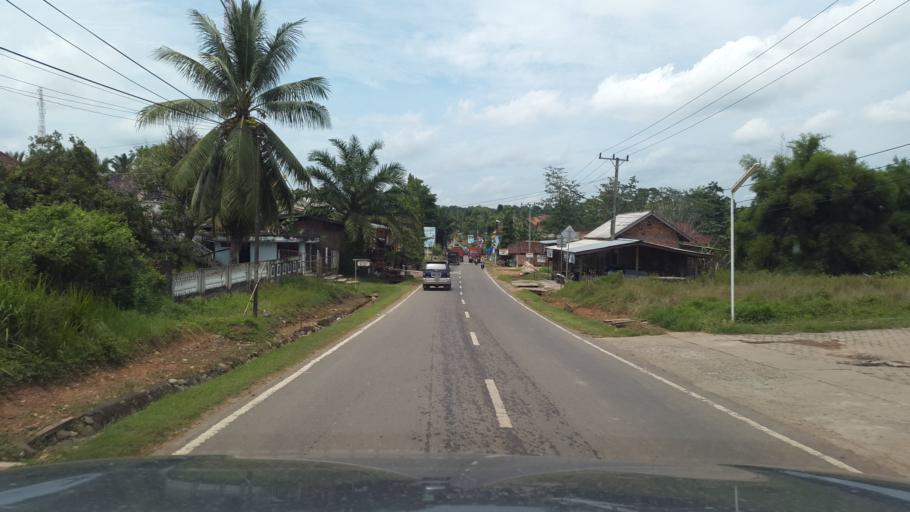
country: ID
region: South Sumatra
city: Gunungmegang Dalam
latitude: -3.2949
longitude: 103.8483
